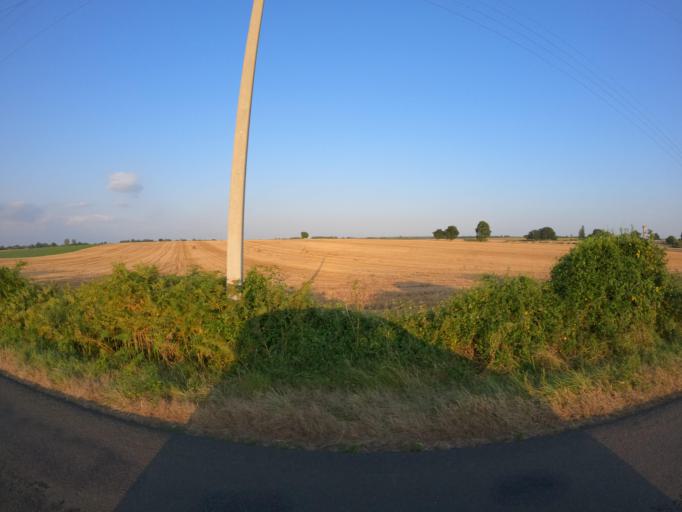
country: FR
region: Pays de la Loire
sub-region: Departement de la Sarthe
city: Parce-sur-Sarthe
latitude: 47.8863
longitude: -0.2201
